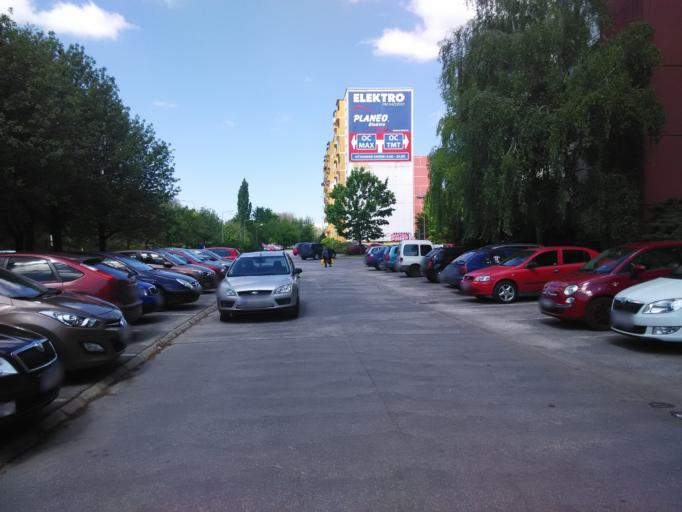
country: SK
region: Trnavsky
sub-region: Okres Trnava
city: Trnava
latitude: 48.3763
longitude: 17.5947
